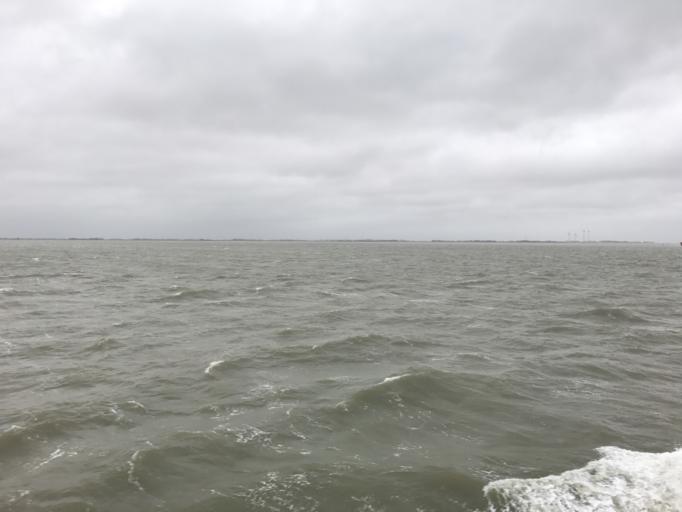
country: NL
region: Groningen
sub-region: Gemeente Delfzijl
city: Delfzijl
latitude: 53.3984
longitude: 6.9509
